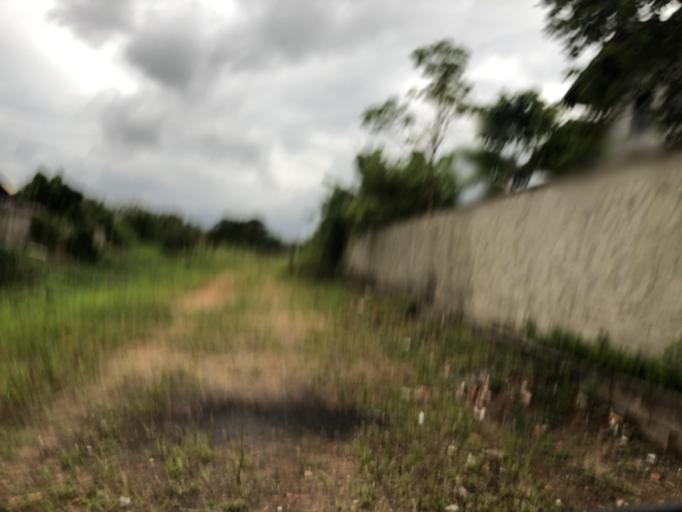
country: BR
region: Santa Catarina
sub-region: Sao Francisco Do Sul
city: Sao Francisco do Sul
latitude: -26.2194
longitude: -48.5326
